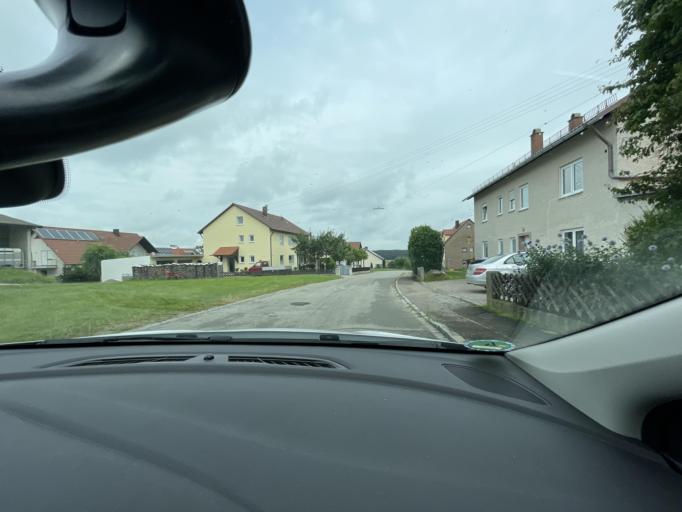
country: DE
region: Bavaria
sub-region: Swabia
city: Aindling
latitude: 48.5627
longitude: 10.9659
